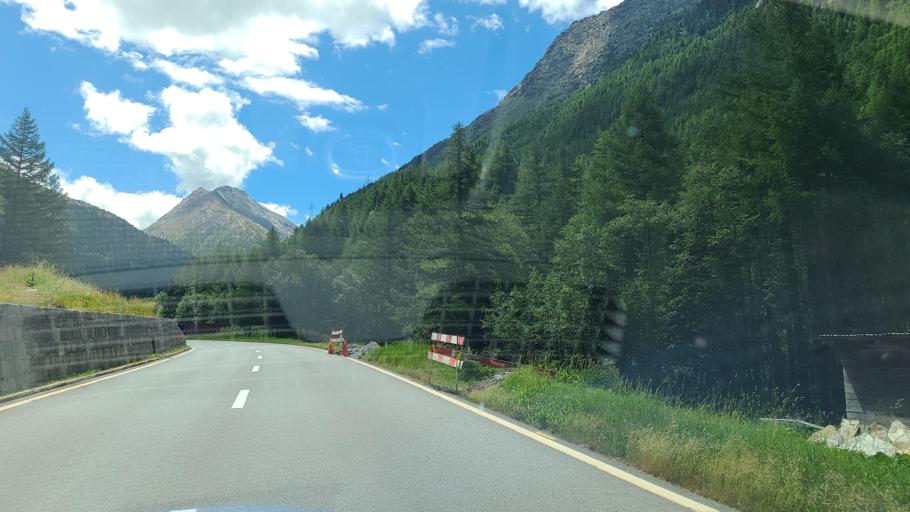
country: CH
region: Valais
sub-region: Visp District
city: Saas-Grund
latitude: 46.1073
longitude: 7.9451
